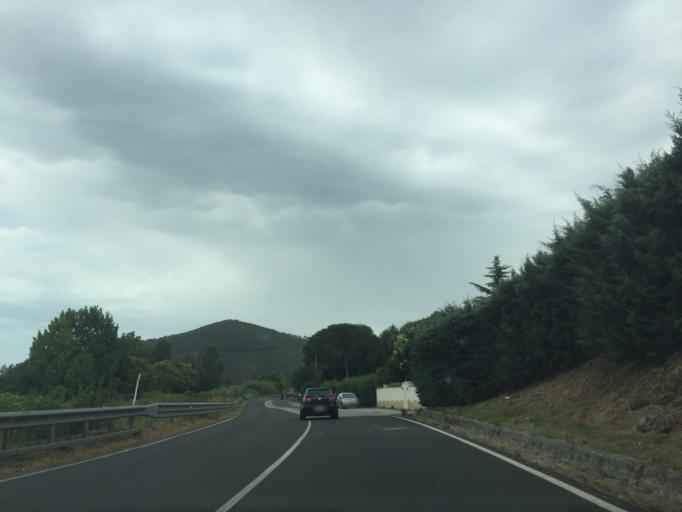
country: IT
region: Tuscany
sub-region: Province of Pisa
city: Asciano
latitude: 43.7422
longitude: 10.4685
